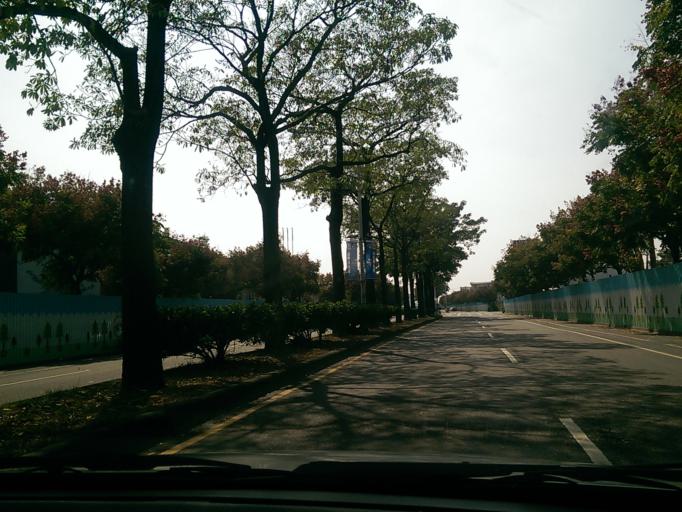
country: TW
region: Taiwan
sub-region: Taichung City
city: Taichung
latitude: 24.1276
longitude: 120.6496
